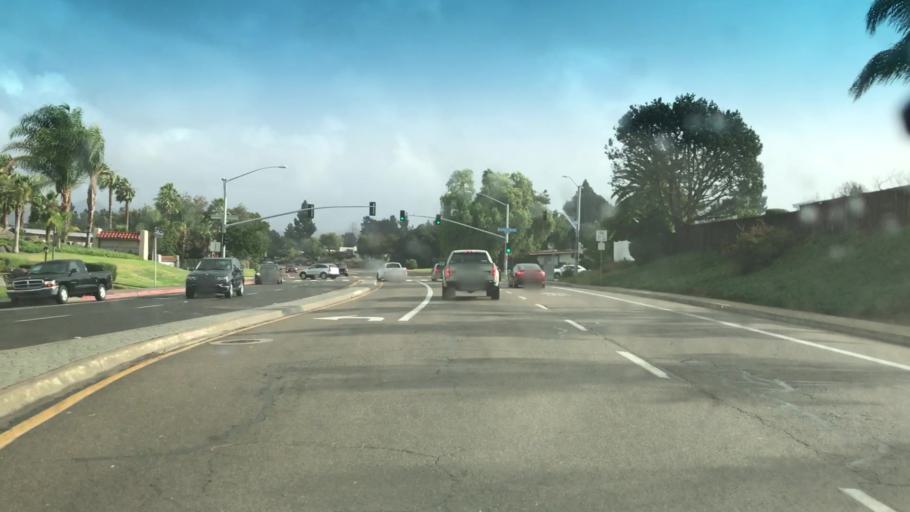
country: US
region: California
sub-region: San Diego County
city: Poway
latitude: 33.0198
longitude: -117.0661
